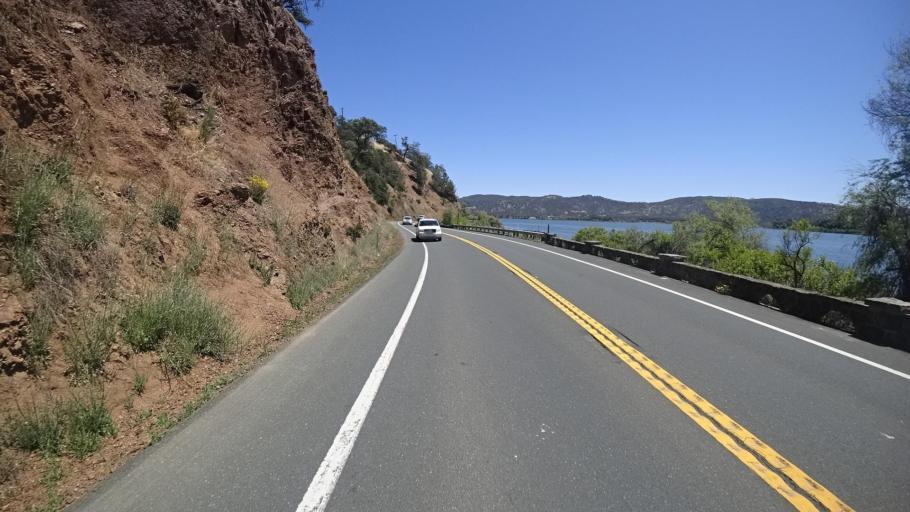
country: US
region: California
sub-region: Lake County
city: Clearlake Oaks
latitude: 39.0206
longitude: -122.6819
